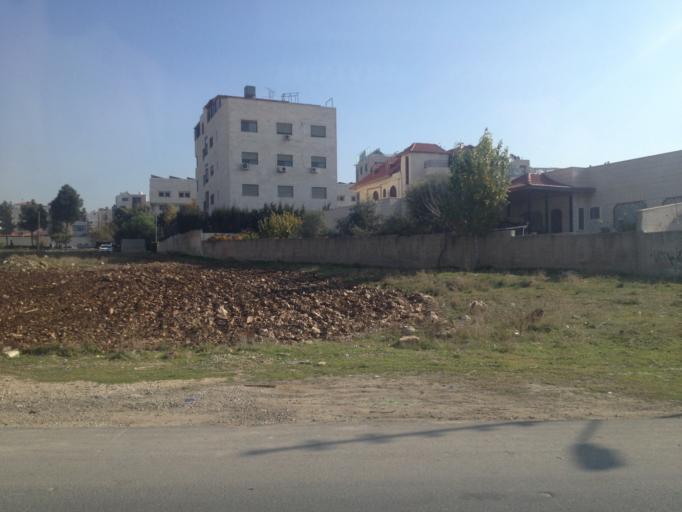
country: JO
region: Amman
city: Wadi as Sir
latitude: 31.9526
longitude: 35.8572
